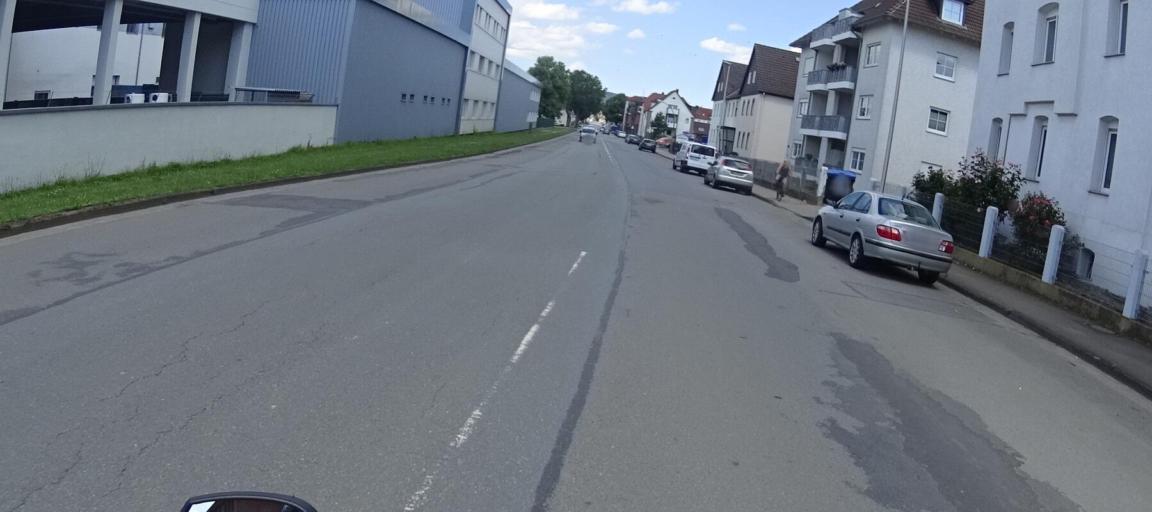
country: DE
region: Lower Saxony
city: Holzminden
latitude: 51.8155
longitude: 9.4489
